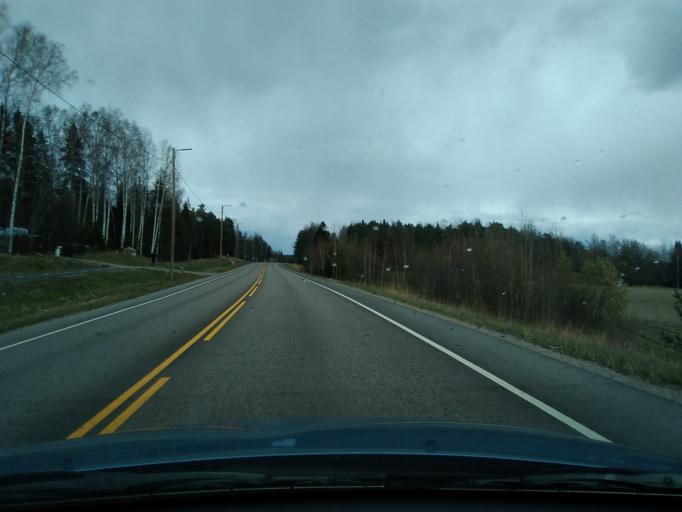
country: FI
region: Uusimaa
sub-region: Porvoo
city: Porvoo
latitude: 60.3593
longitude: 25.5358
